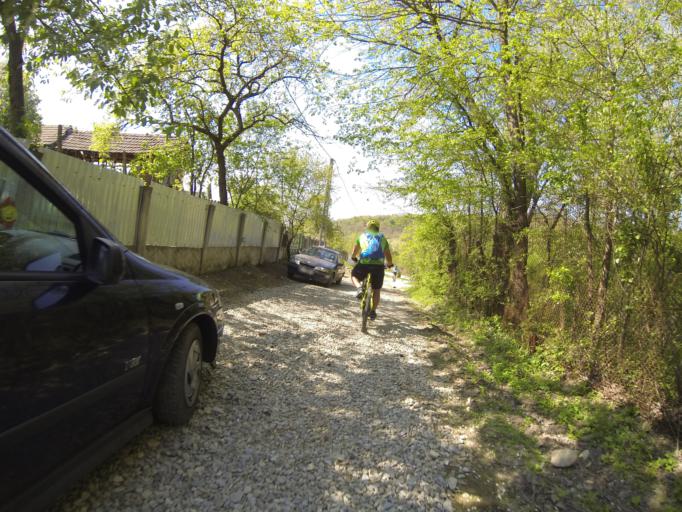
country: RO
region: Gorj
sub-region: Comuna Crusetu
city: Crusetu
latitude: 44.6167
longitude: 23.6524
